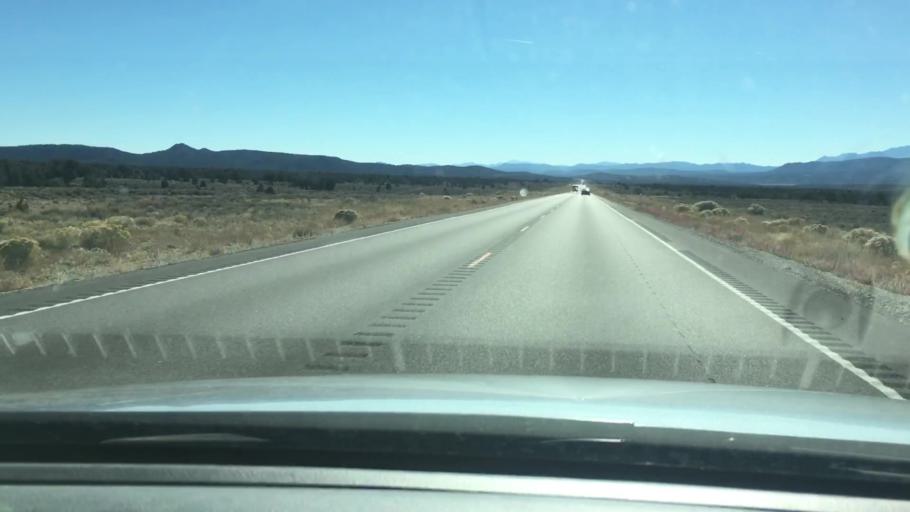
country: US
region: Nevada
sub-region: White Pine County
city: Ely
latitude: 39.1503
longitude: -115.0334
